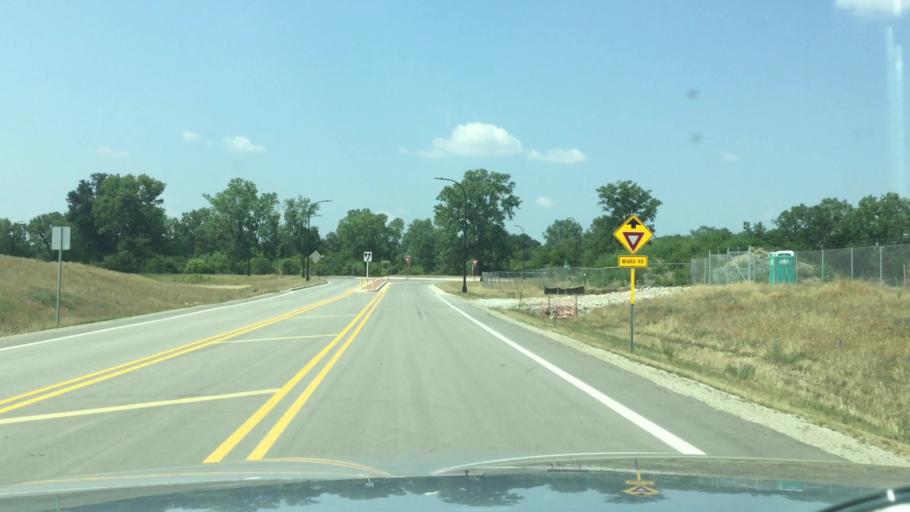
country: US
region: Michigan
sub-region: Washtenaw County
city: Ypsilanti
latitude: 42.2379
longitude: -83.5614
